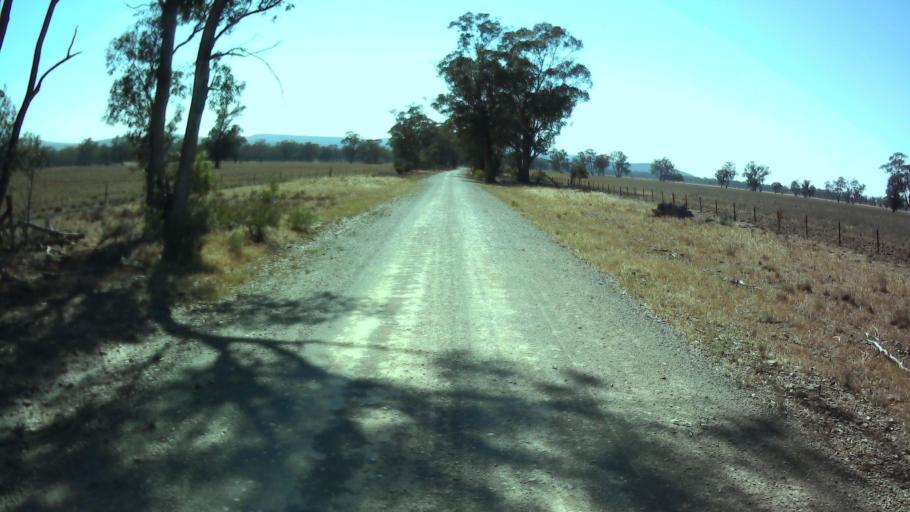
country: AU
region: New South Wales
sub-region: Weddin
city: Grenfell
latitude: -33.9443
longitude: 147.8633
